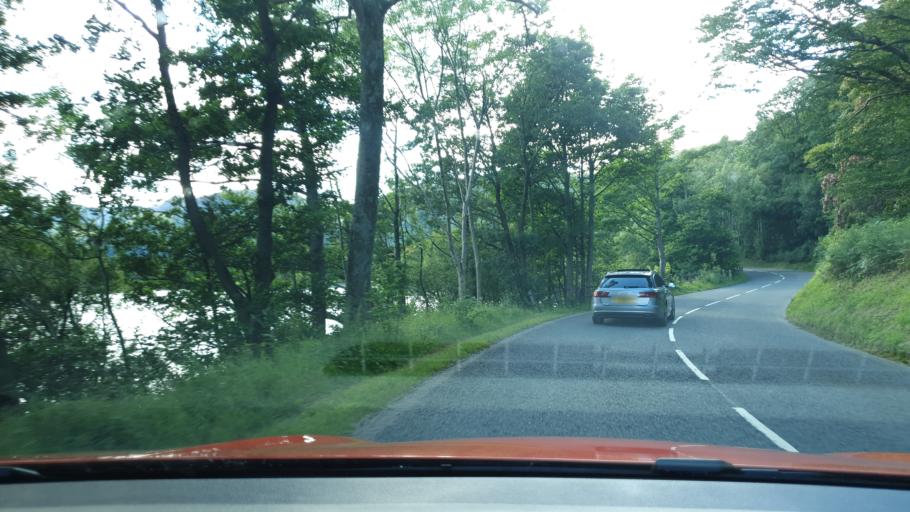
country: GB
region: England
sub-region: Cumbria
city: Ambleside
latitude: 54.5733
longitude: -2.9182
